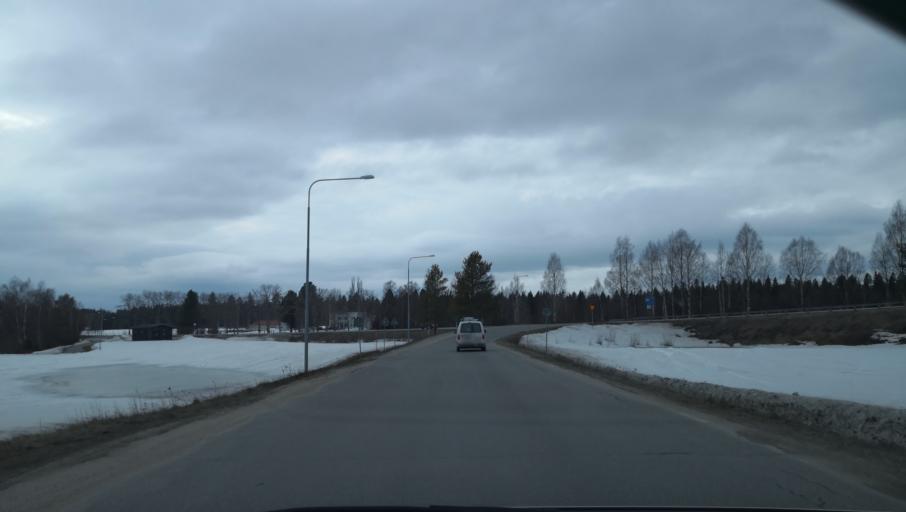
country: SE
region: Vaesterbotten
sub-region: Vannas Kommun
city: Vaennaes
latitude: 63.9194
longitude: 19.7825
